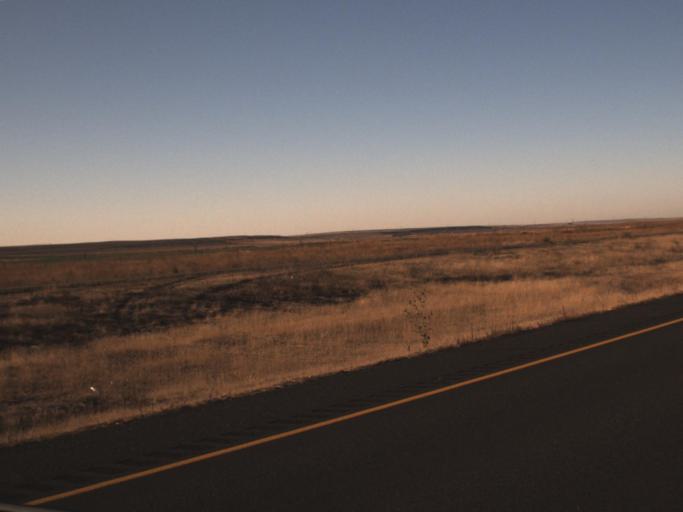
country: US
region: Washington
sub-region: Franklin County
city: Connell
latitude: 46.6202
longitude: -118.8981
